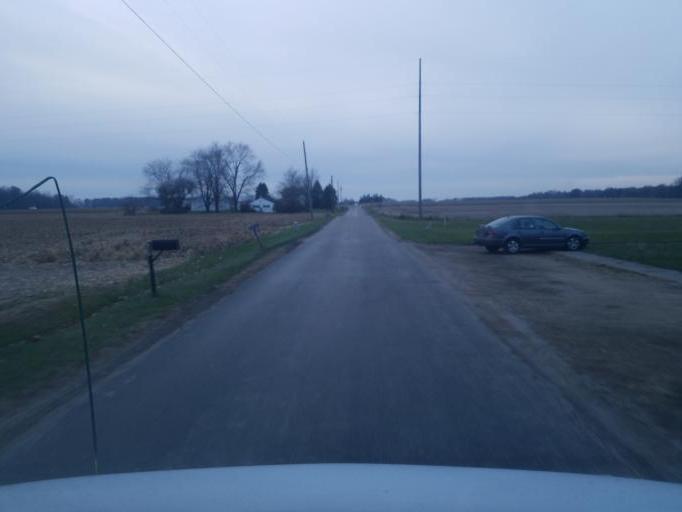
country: US
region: Indiana
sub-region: Adams County
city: Decatur
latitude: 40.7887
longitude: -84.9331
